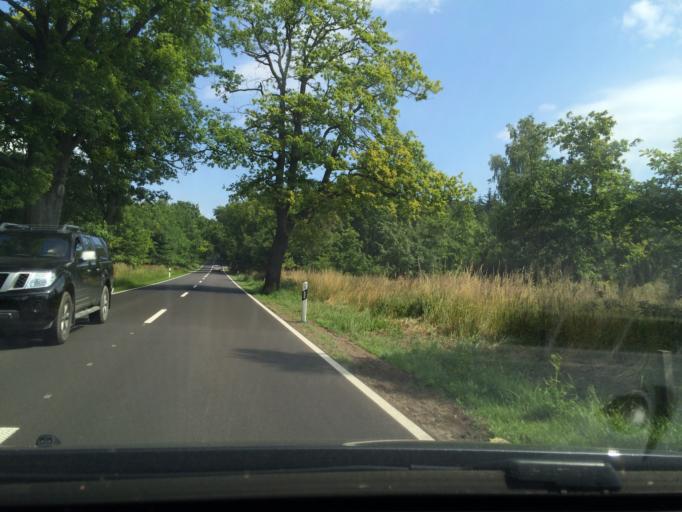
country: DE
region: Mecklenburg-Vorpommern
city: Ostseebad Binz
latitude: 54.4276
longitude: 13.5492
